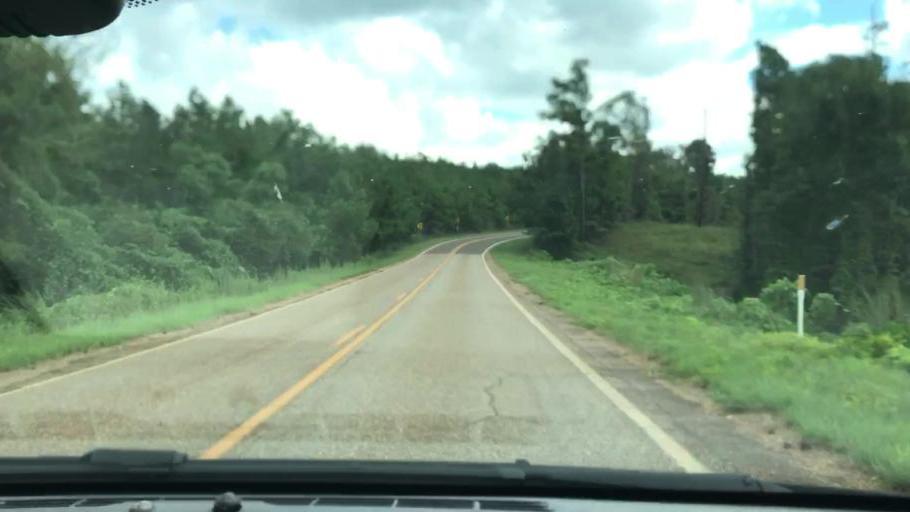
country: US
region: Georgia
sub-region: Stewart County
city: Lumpkin
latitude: 32.0726
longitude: -84.8781
